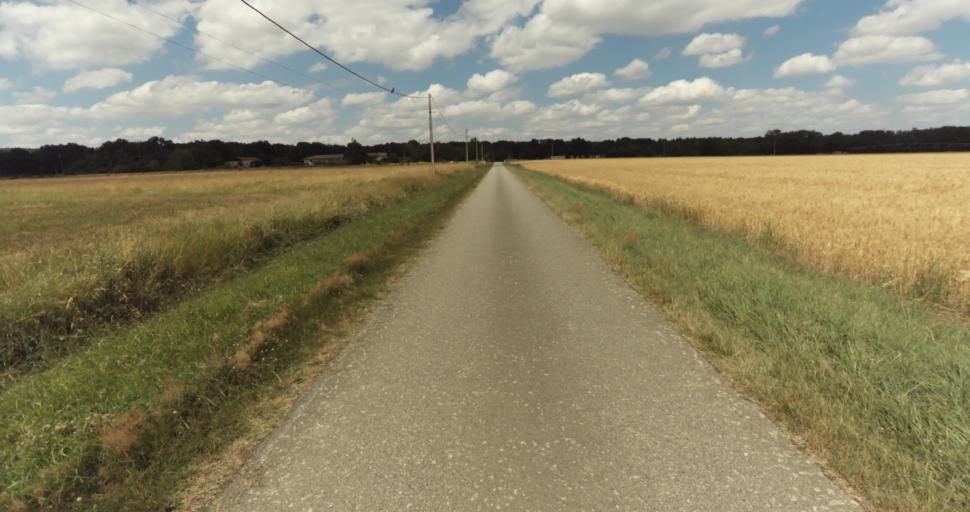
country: FR
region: Midi-Pyrenees
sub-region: Departement de la Haute-Garonne
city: Fontenilles
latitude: 43.5663
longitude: 1.1788
